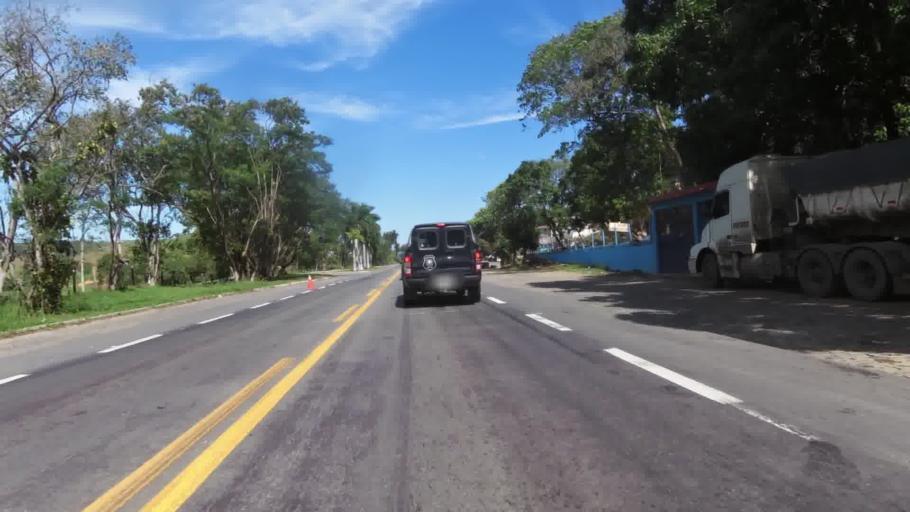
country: BR
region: Espirito Santo
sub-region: Viana
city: Viana
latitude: -20.4084
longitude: -40.4585
